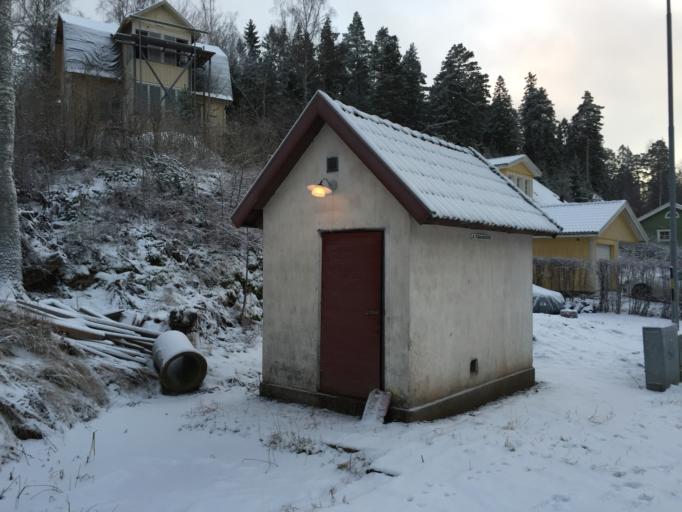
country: SE
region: Stockholm
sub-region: Salems Kommun
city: Ronninge
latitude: 59.1887
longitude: 17.7594
